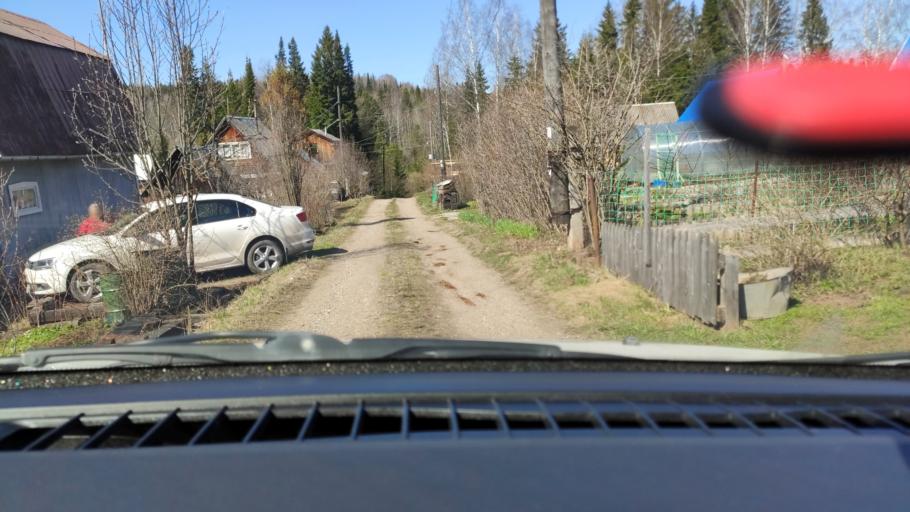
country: RU
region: Perm
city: Bershet'
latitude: 57.7220
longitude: 56.4097
